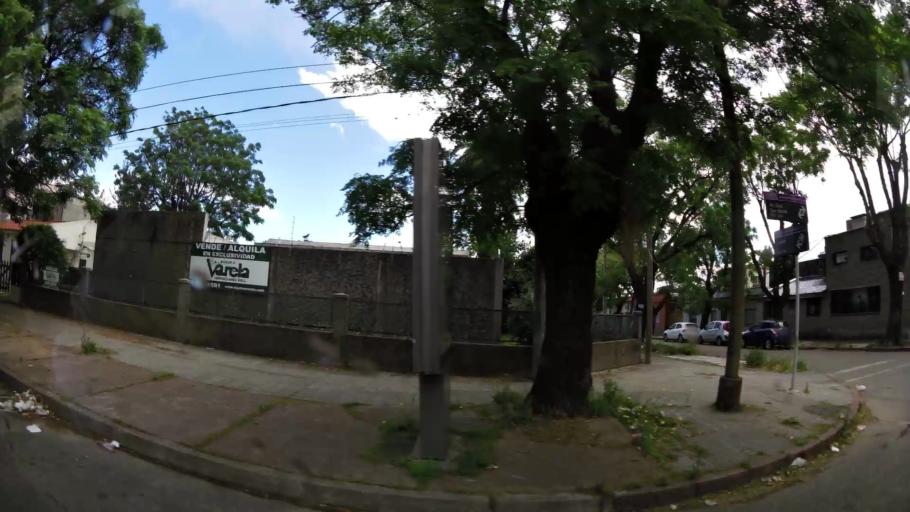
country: UY
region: Montevideo
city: Montevideo
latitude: -34.8673
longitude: -56.1809
